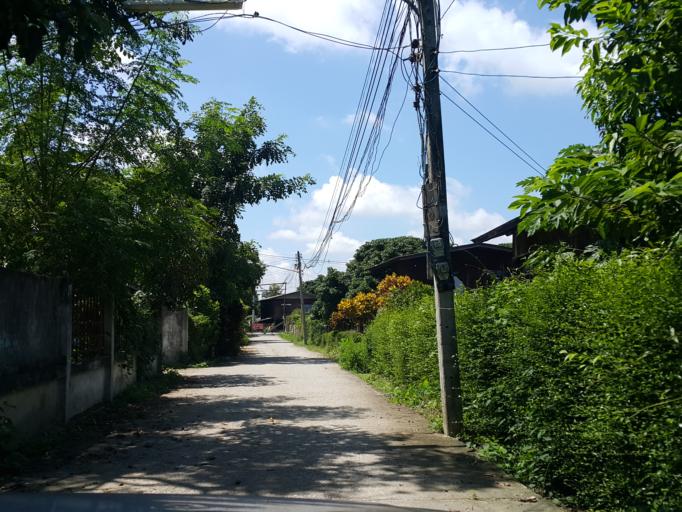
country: TH
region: Chiang Mai
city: San Kamphaeng
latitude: 18.6951
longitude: 99.1155
